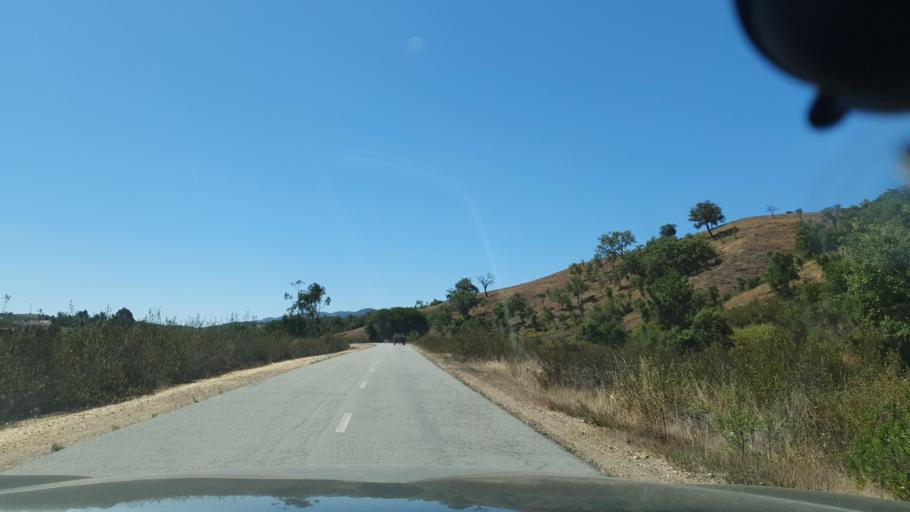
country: PT
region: Beja
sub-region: Odemira
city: Sao Teotonio
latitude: 37.4808
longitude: -8.6307
